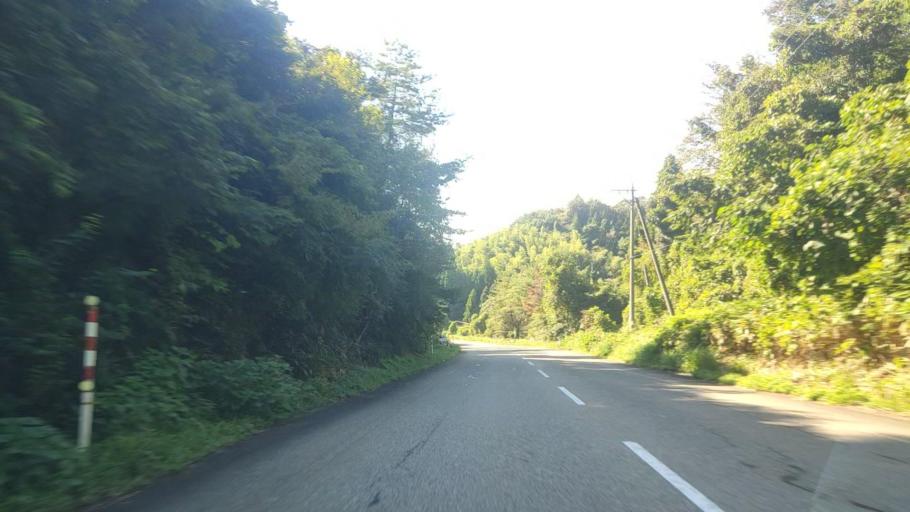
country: JP
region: Ishikawa
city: Nanao
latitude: 37.3150
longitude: 137.1533
